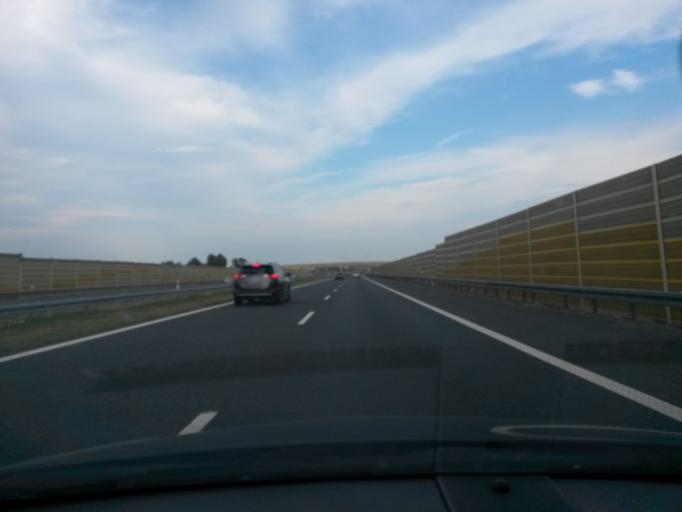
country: PL
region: Lodz Voivodeship
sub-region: Powiat poddebicki
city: Wartkowice
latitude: 51.9970
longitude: 19.0257
